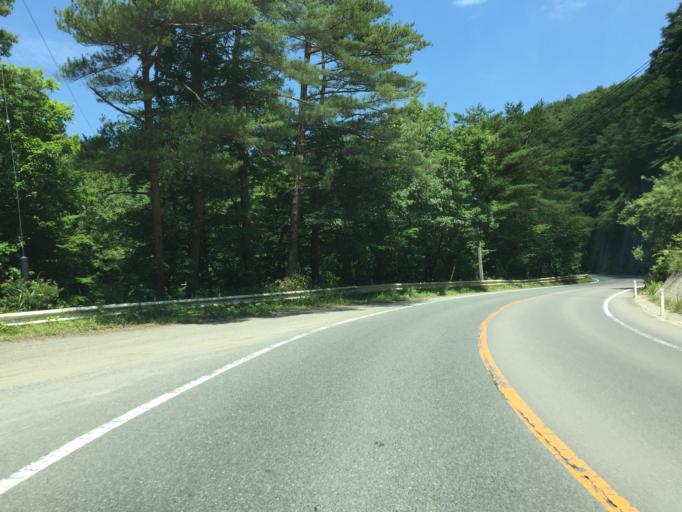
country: JP
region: Miyagi
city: Marumori
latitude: 37.7729
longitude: 140.7668
